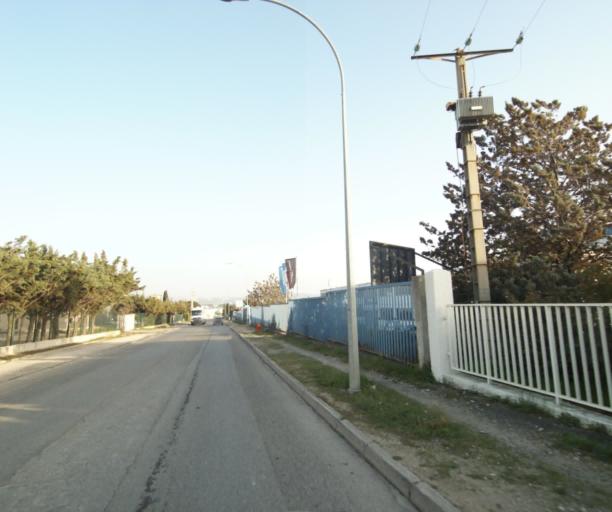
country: FR
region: Provence-Alpes-Cote d'Azur
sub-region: Departement des Bouches-du-Rhone
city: Vitrolles
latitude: 43.4378
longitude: 5.2473
